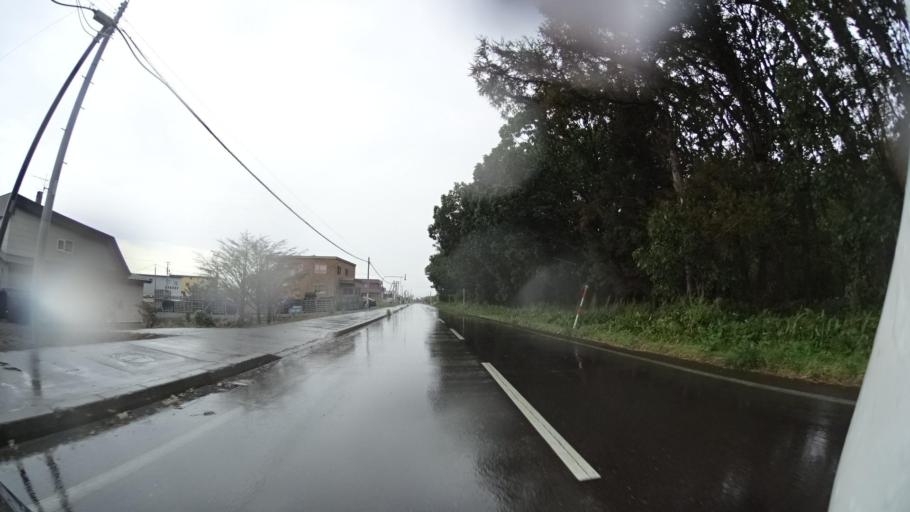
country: JP
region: Hokkaido
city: Kitami
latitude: 44.1887
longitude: 143.7465
